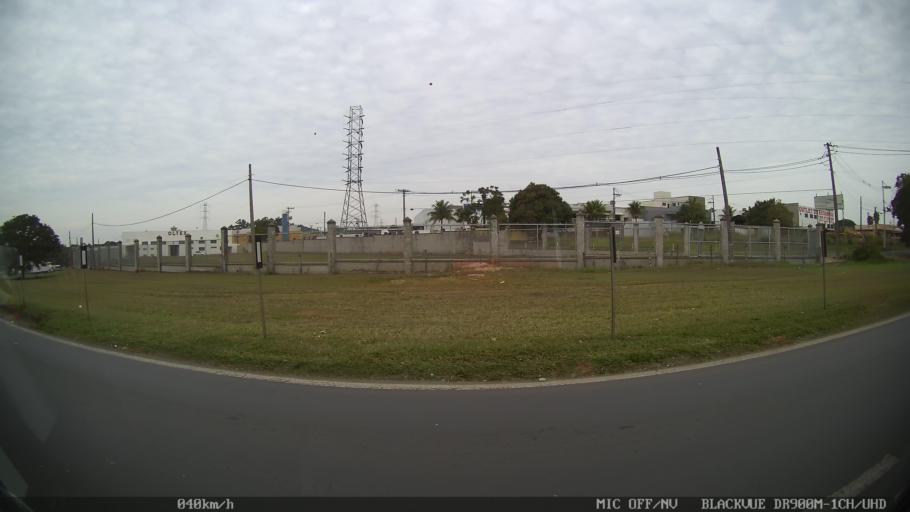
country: BR
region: Sao Paulo
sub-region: Americana
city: Americana
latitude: -22.7286
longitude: -47.2947
